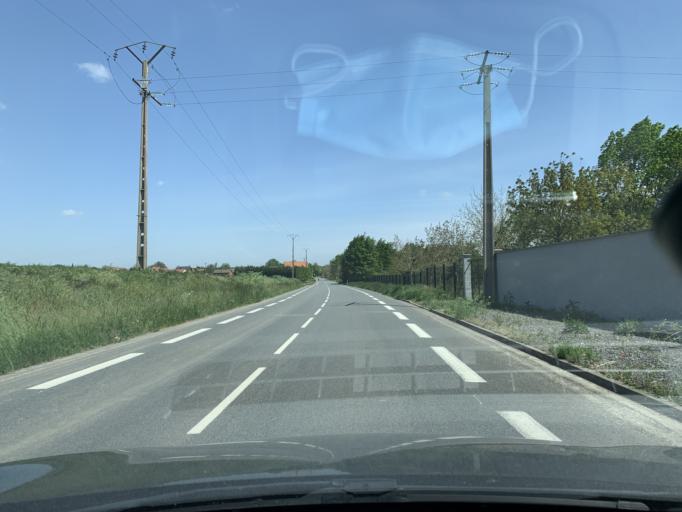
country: FR
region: Nord-Pas-de-Calais
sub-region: Departement du Nord
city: Masnieres
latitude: 50.1182
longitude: 3.1922
